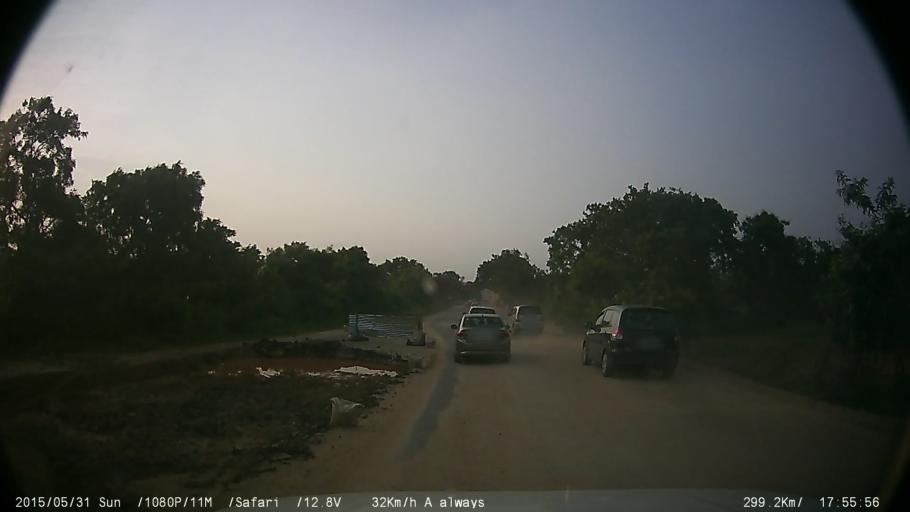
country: IN
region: Karnataka
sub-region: Mysore
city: Nanjangud
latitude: 11.9932
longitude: 76.6698
